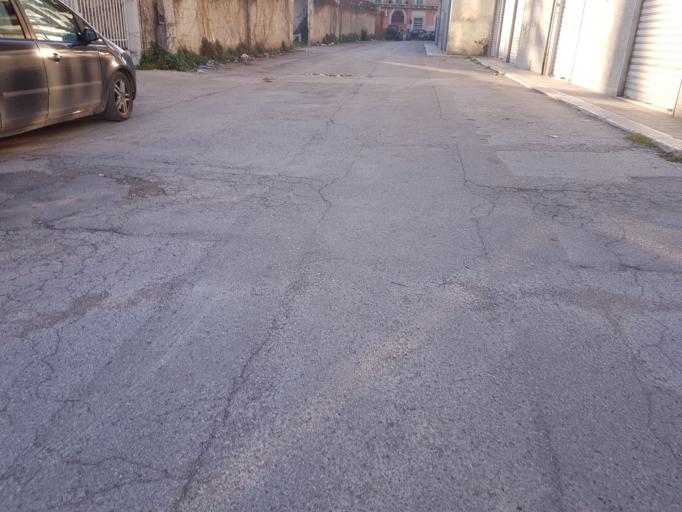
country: IT
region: Apulia
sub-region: Provincia di Bari
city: Corato
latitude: 41.1477
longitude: 16.4084
